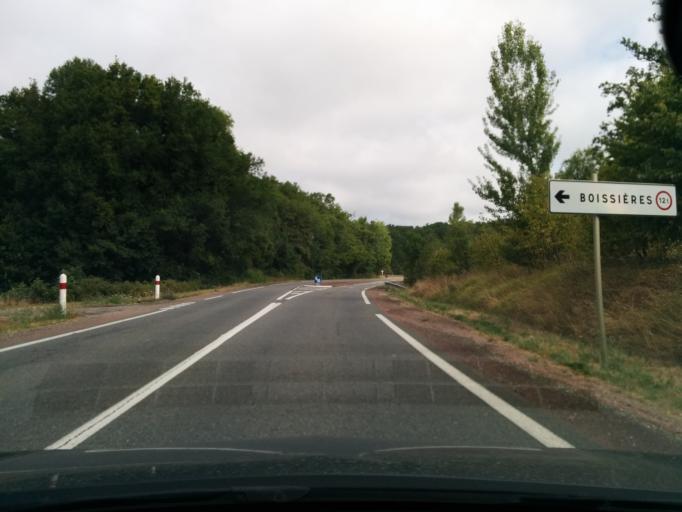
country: FR
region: Midi-Pyrenees
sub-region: Departement du Lot
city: Pradines
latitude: 44.5642
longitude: 1.4722
